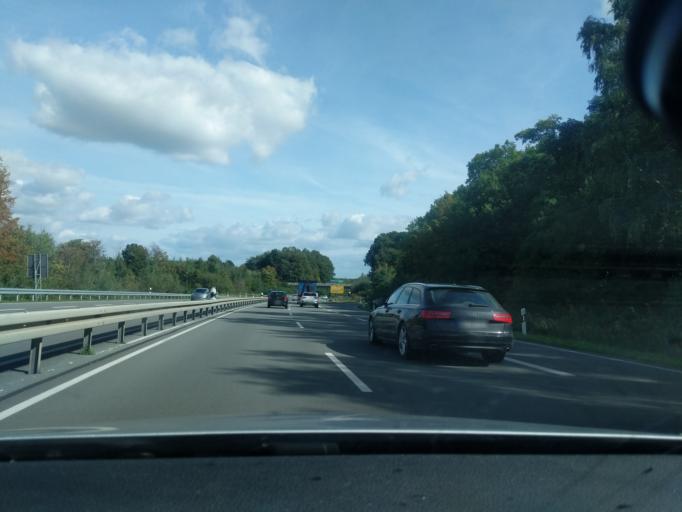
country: DE
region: Lower Saxony
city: Ostercappeln
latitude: 52.3392
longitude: 8.2148
